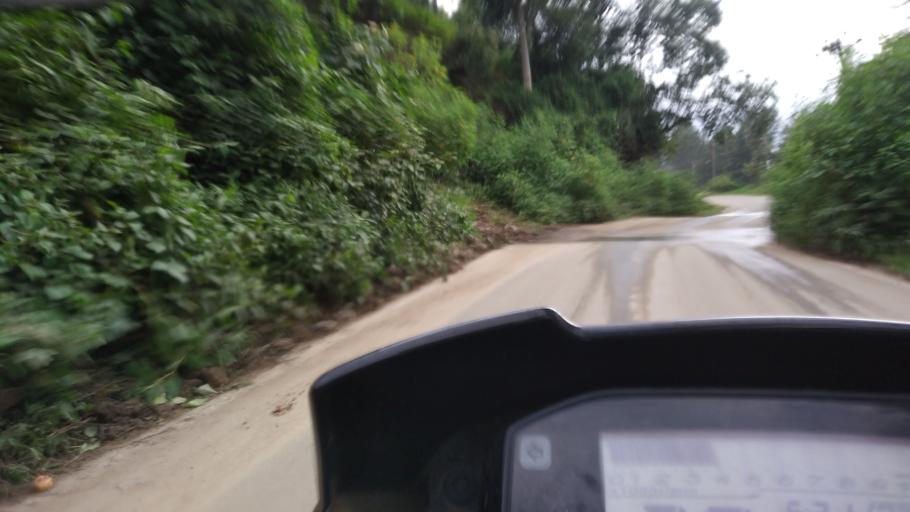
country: IN
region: Tamil Nadu
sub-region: Theni
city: Bodinayakkanur
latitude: 10.0161
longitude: 77.2418
